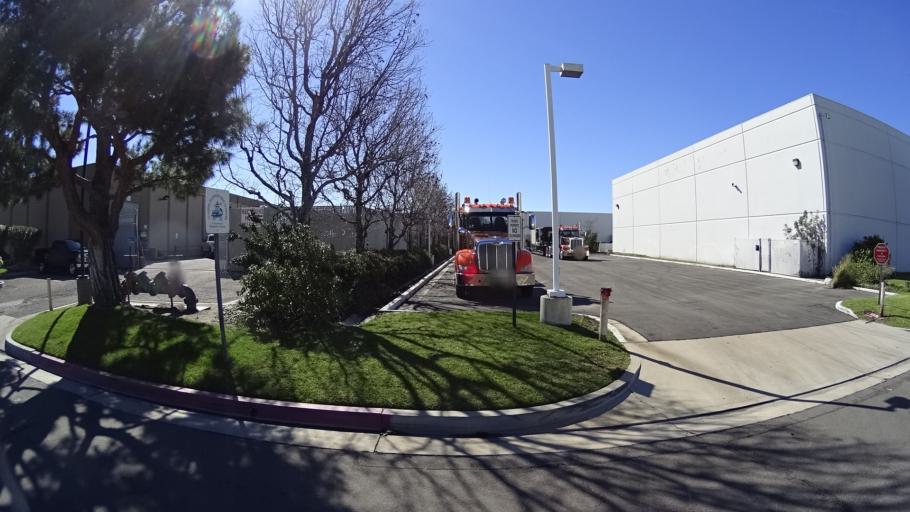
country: US
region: California
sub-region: Orange County
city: Yorba Linda
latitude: 33.8640
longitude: -117.8129
